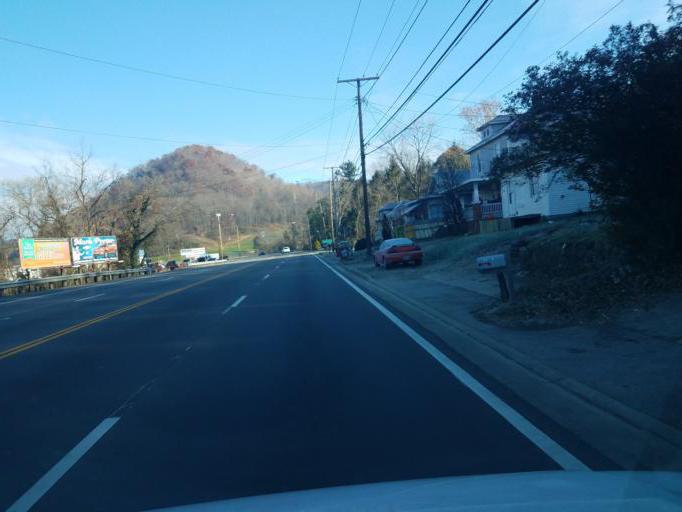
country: US
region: Ohio
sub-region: Scioto County
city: Rosemount
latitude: 38.7671
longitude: -82.9874
